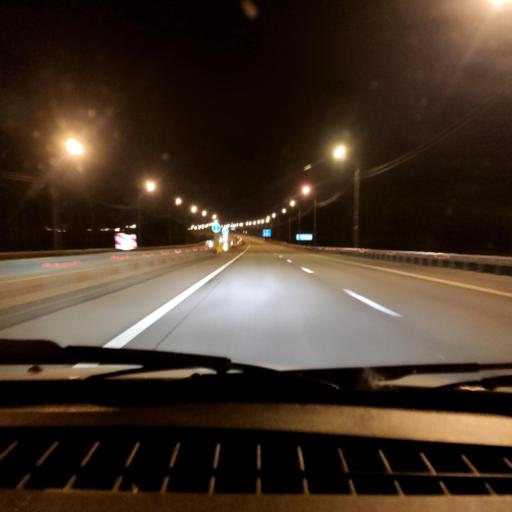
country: RU
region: Lipetsk
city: Zadonsk
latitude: 52.3236
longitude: 39.0289
